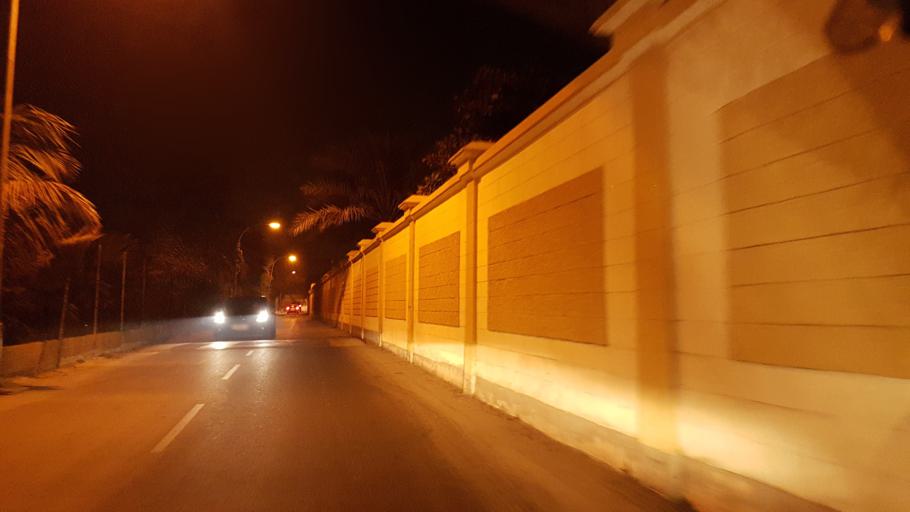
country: BH
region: Manama
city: Jidd Hafs
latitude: 26.2225
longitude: 50.4933
